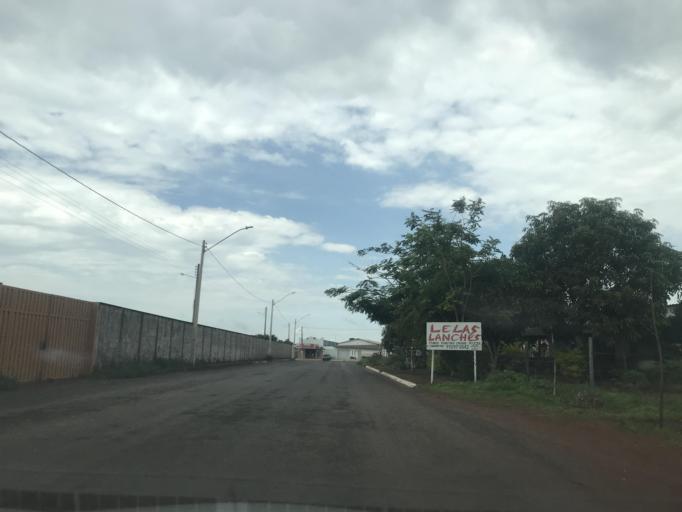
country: BR
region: Goias
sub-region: Luziania
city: Luziania
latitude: -16.2577
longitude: -47.9744
